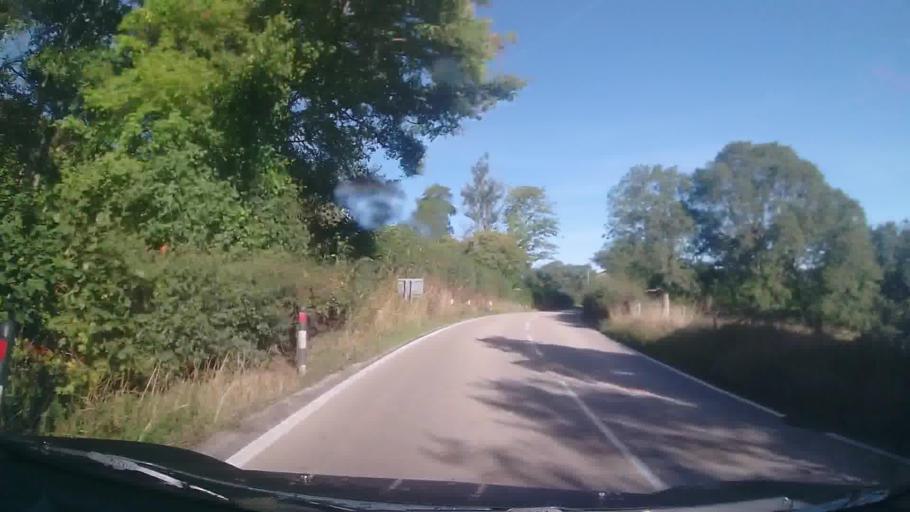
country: GB
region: Wales
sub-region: Sir Powys
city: Hay
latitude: 51.9466
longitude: -3.1898
